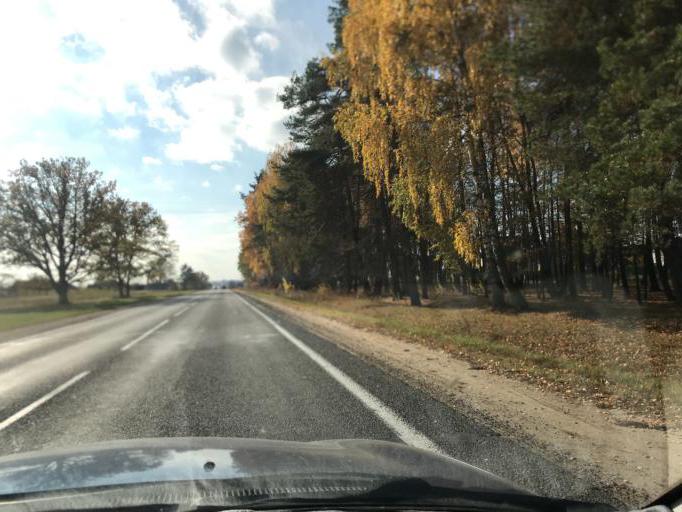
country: BY
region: Grodnenskaya
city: Voranava
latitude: 54.1644
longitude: 25.3291
